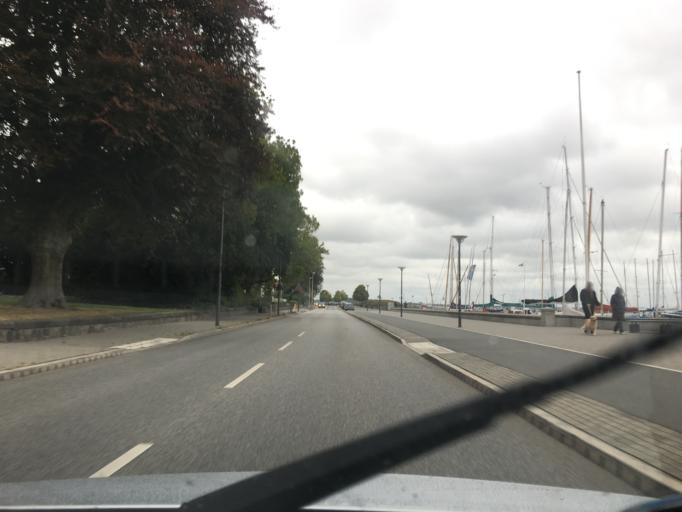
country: DE
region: Schleswig-Holstein
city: Kiel
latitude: 54.3388
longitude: 10.1569
